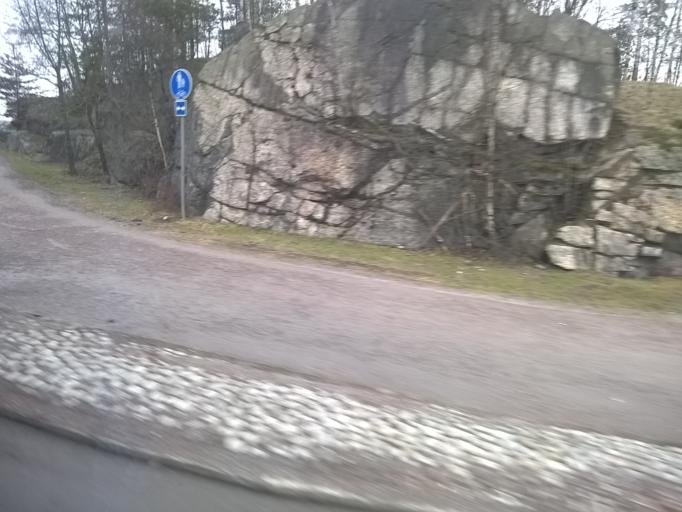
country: FI
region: Pirkanmaa
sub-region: Tampere
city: Tampere
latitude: 61.4537
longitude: 23.8473
